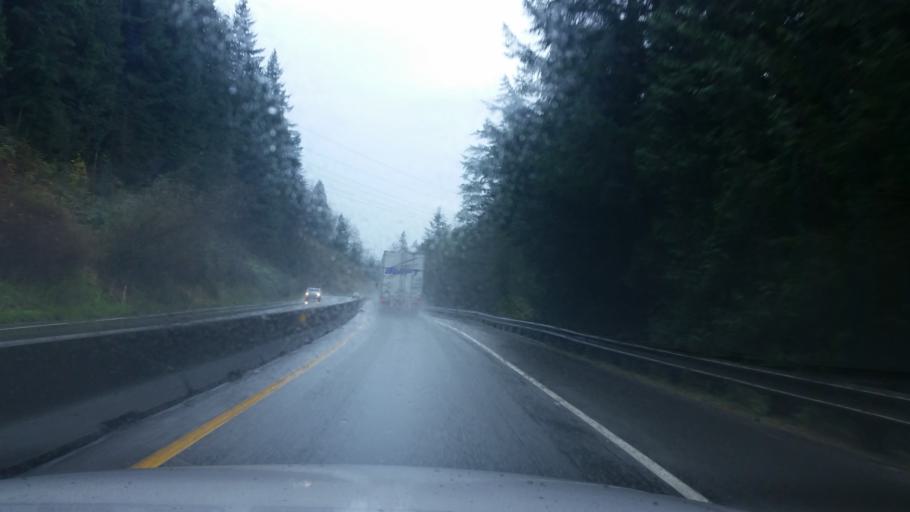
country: US
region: Washington
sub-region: King County
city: Hobart
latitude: 47.4601
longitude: -121.9478
